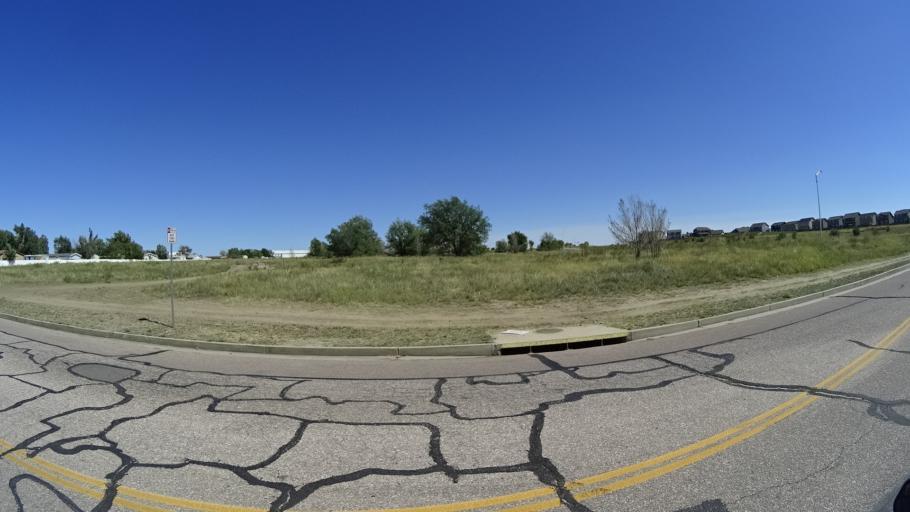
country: US
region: Colorado
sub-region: El Paso County
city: Security-Widefield
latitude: 38.7895
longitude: -104.7336
